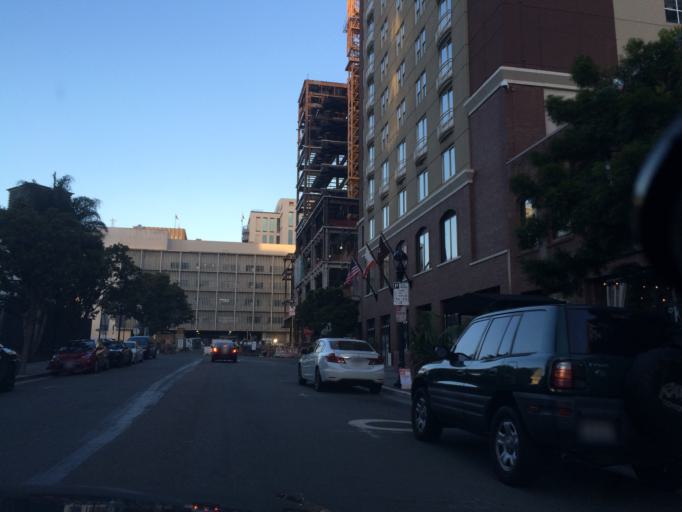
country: US
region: California
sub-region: San Diego County
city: San Diego
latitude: 32.7178
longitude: -117.1673
